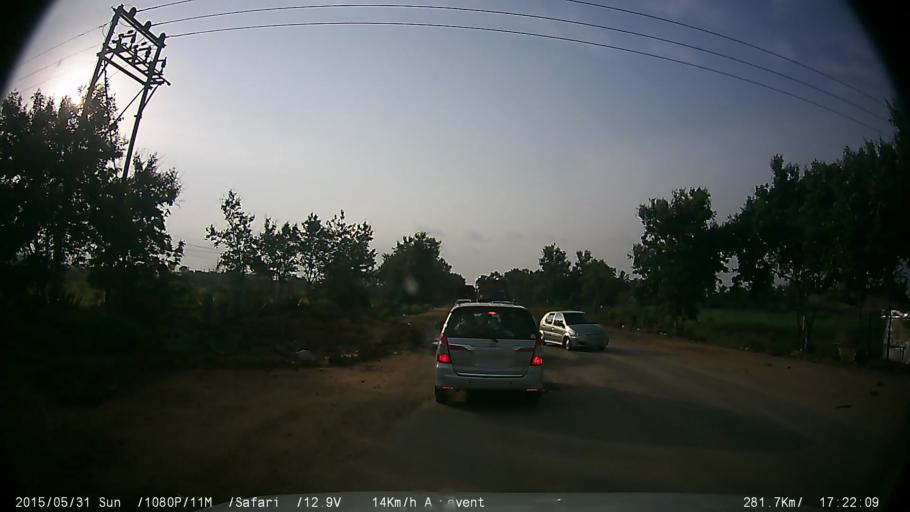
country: IN
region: Karnataka
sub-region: Chamrajnagar
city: Gundlupet
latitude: 11.8312
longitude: 76.6780
